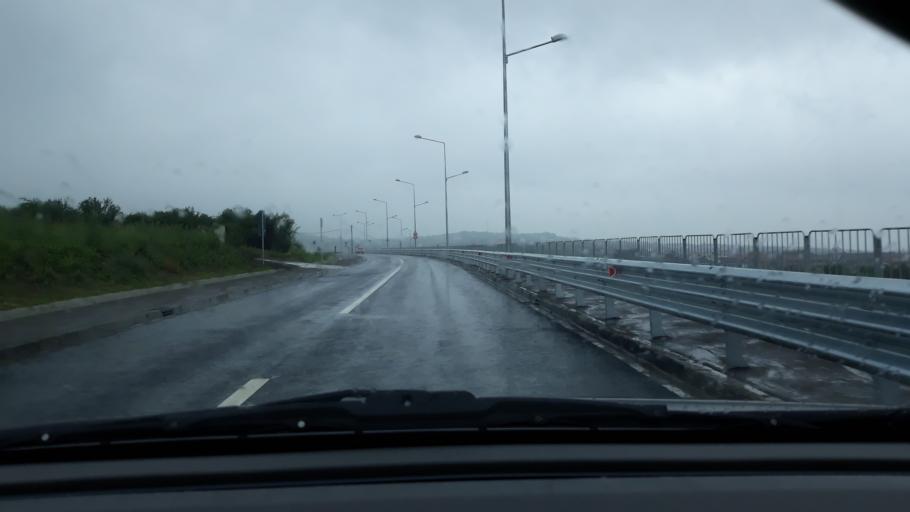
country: RO
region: Bihor
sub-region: Comuna Biharea
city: Oradea
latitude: 47.0978
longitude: 21.9201
